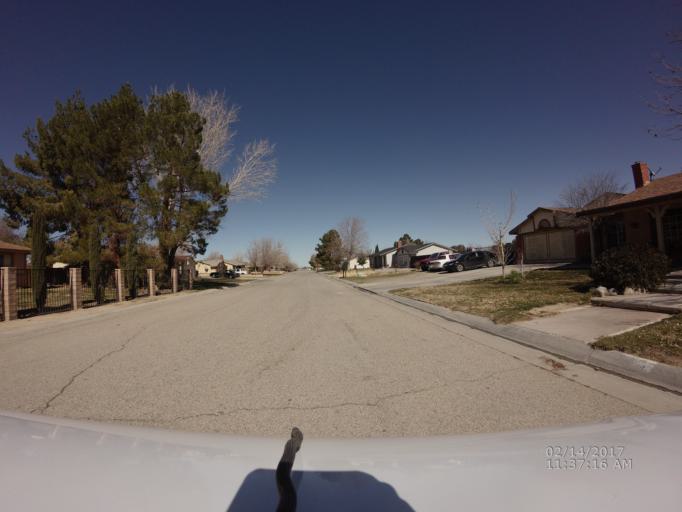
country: US
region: California
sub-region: Los Angeles County
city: Littlerock
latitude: 34.5624
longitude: -117.9559
